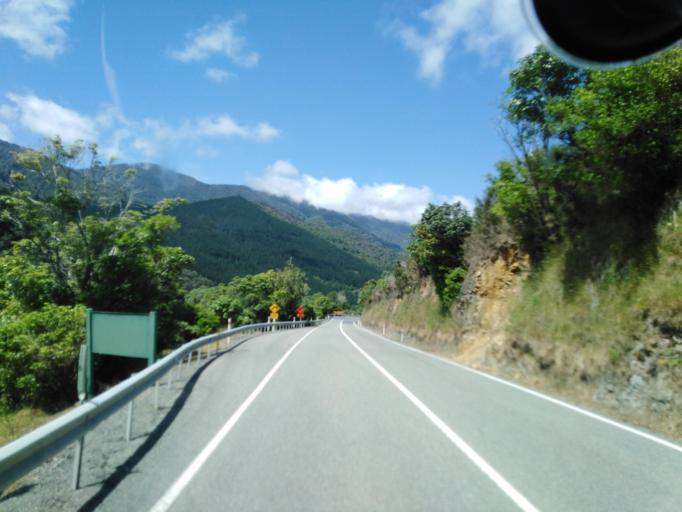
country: NZ
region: Nelson
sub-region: Nelson City
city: Nelson
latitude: -41.2272
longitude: 173.4360
